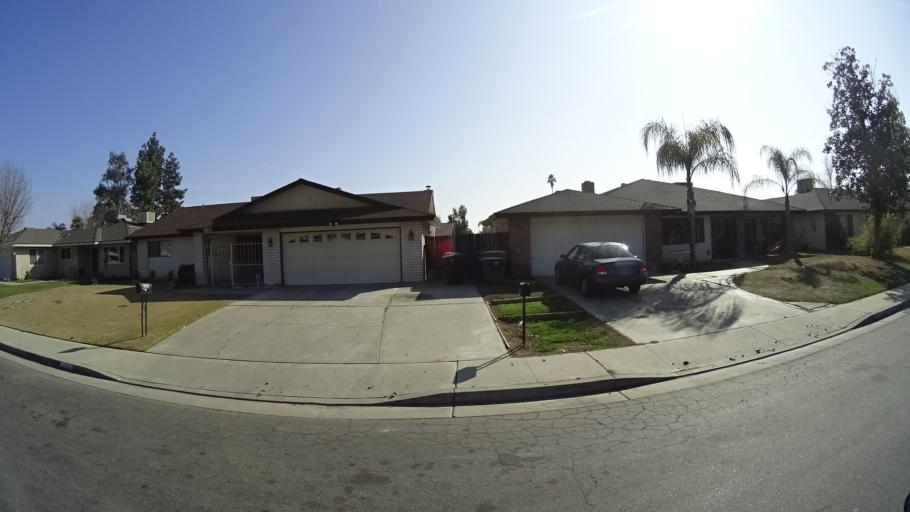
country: US
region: California
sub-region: Kern County
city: Bakersfield
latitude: 35.3372
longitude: -119.0586
